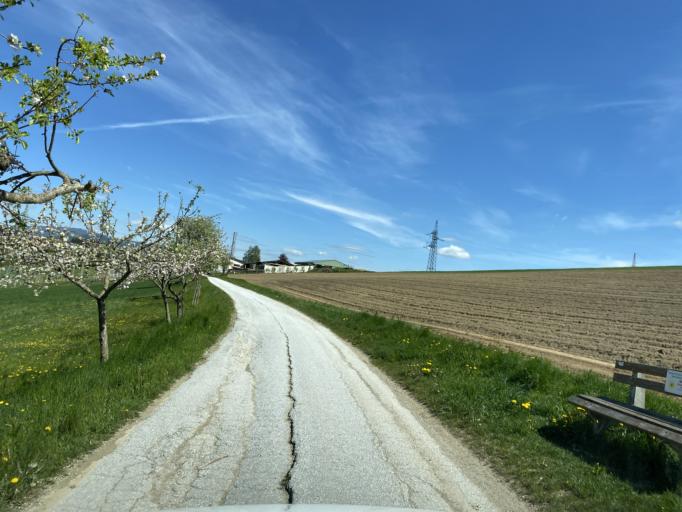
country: AT
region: Styria
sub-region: Politischer Bezirk Weiz
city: Birkfeld
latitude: 47.3428
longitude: 15.6916
